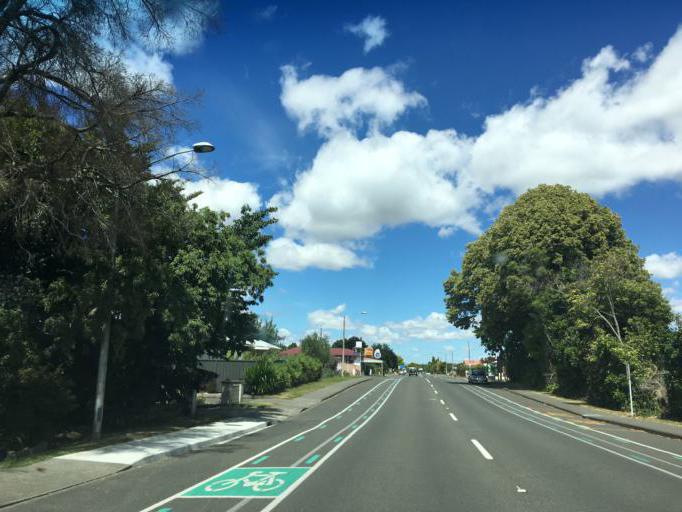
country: NZ
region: Hawke's Bay
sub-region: Hastings District
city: Hastings
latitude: -39.6490
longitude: 176.8617
